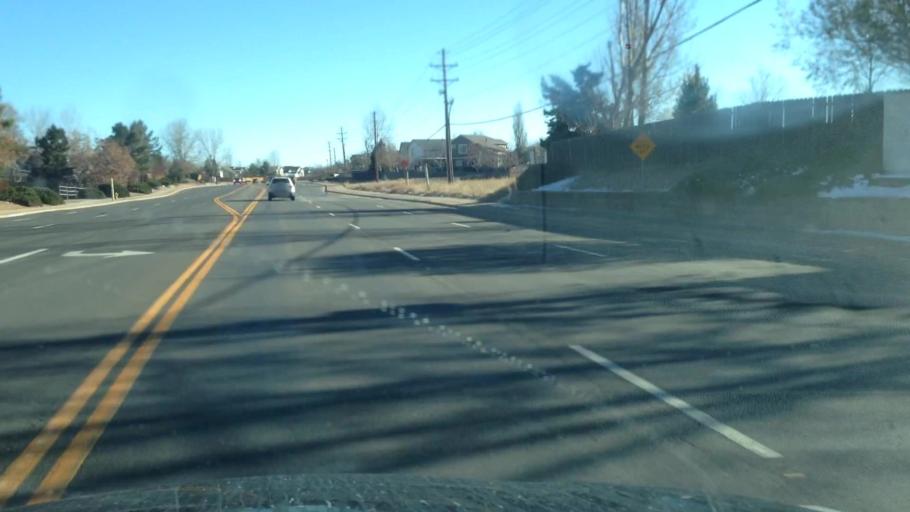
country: US
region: Colorado
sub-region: Douglas County
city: Stonegate
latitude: 39.5617
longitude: -104.7980
